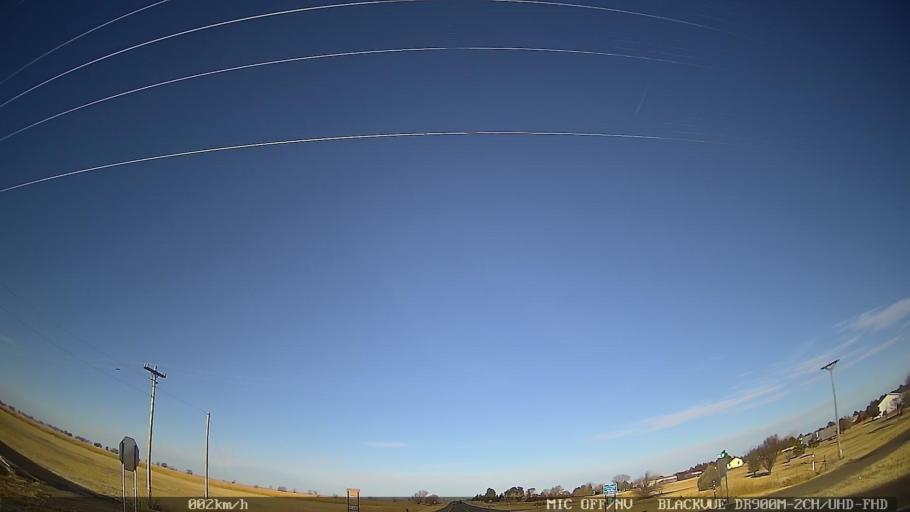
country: US
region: New Mexico
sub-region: Curry County
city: Clovis
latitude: 34.4340
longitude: -103.2486
